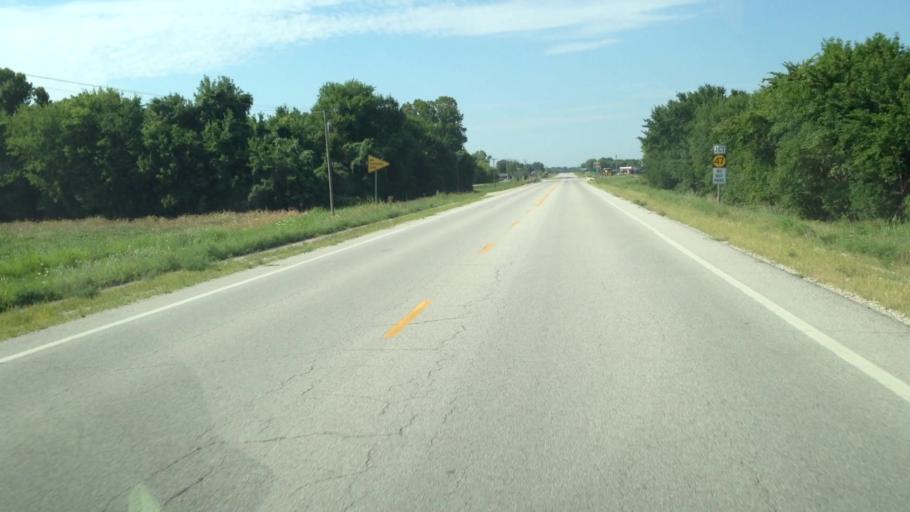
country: US
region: Kansas
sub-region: Neosho County
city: Erie
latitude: 37.5121
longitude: -95.2699
